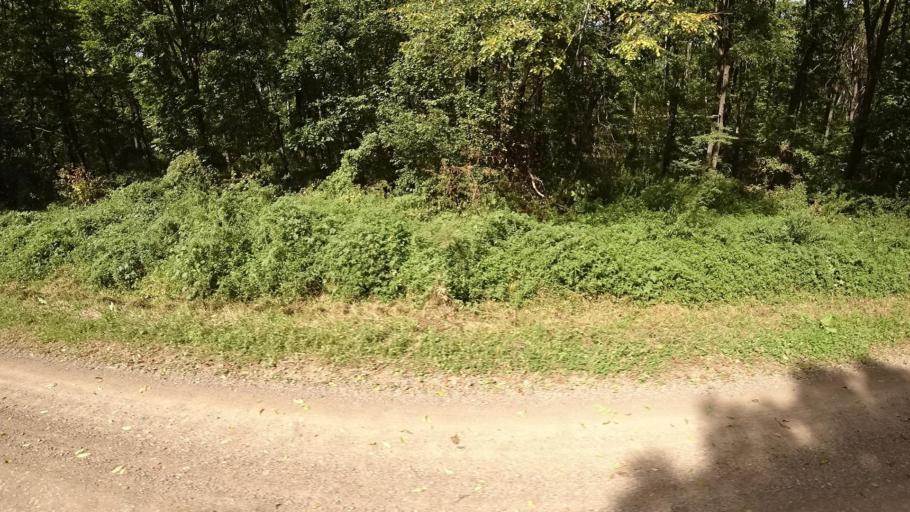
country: RU
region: Primorskiy
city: Yakovlevka
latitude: 44.6595
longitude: 133.7479
